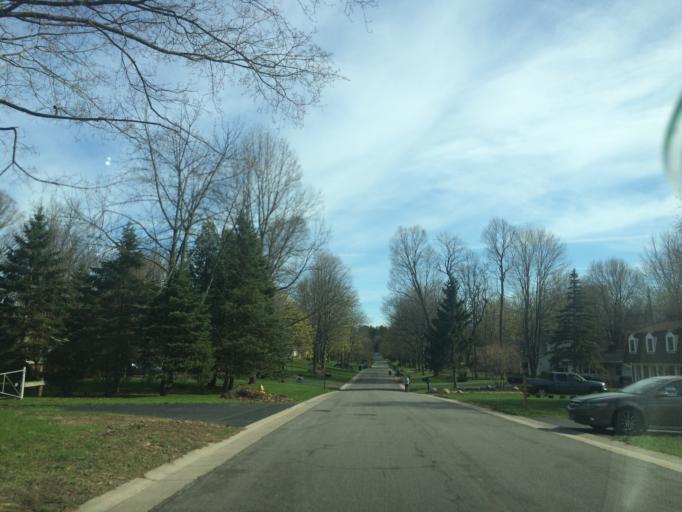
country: US
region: New York
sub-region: Monroe County
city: East Rochester
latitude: 43.0931
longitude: -77.4678
